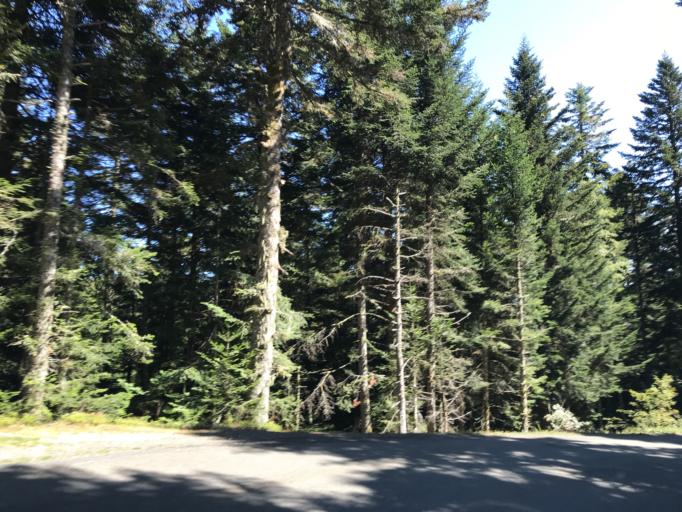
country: FR
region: Rhone-Alpes
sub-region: Departement de la Loire
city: Noiretable
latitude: 45.7914
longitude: 3.7243
